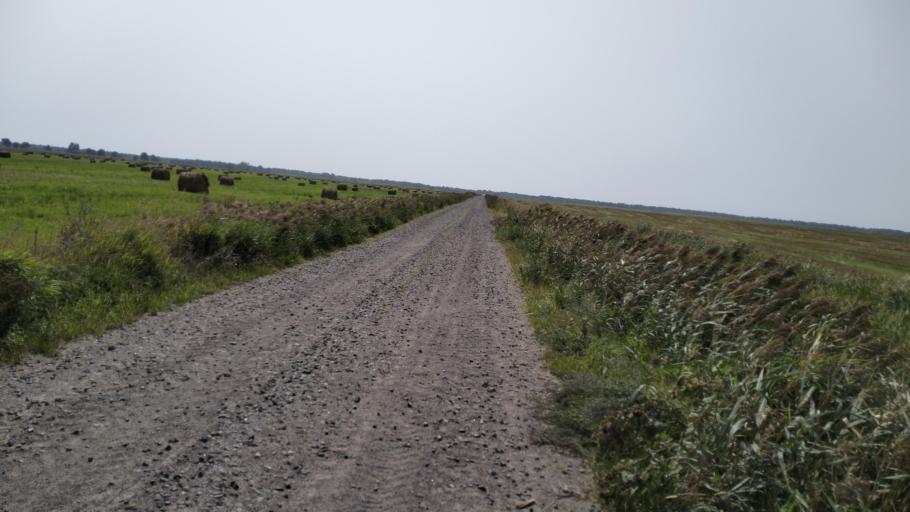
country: BY
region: Brest
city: Davyd-Haradok
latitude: 51.9932
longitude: 27.1762
